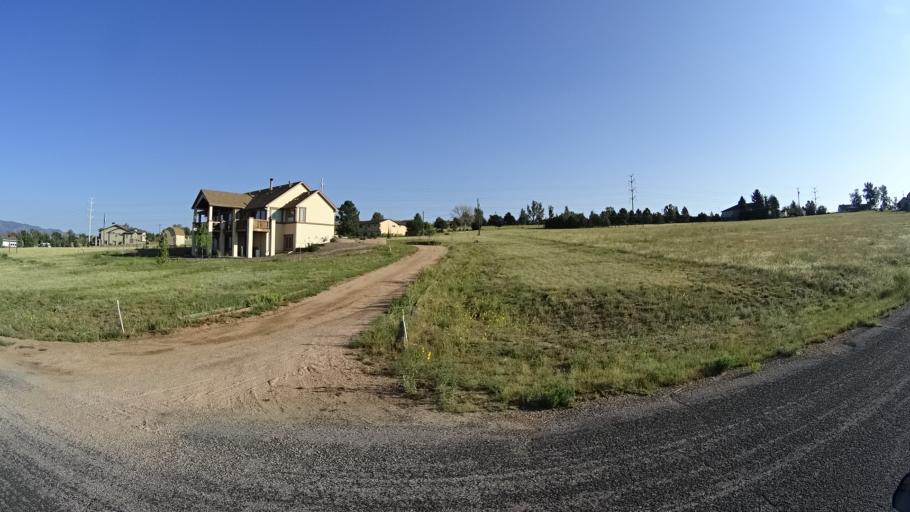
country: US
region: Colorado
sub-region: El Paso County
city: Black Forest
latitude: 38.9384
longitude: -104.7727
